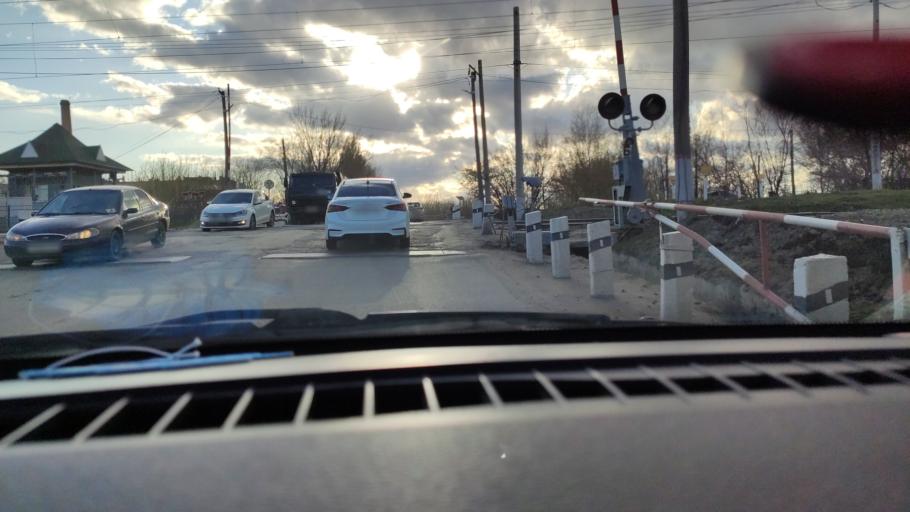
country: RU
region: Saratov
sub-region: Saratovskiy Rayon
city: Saratov
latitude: 51.6150
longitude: 45.9580
